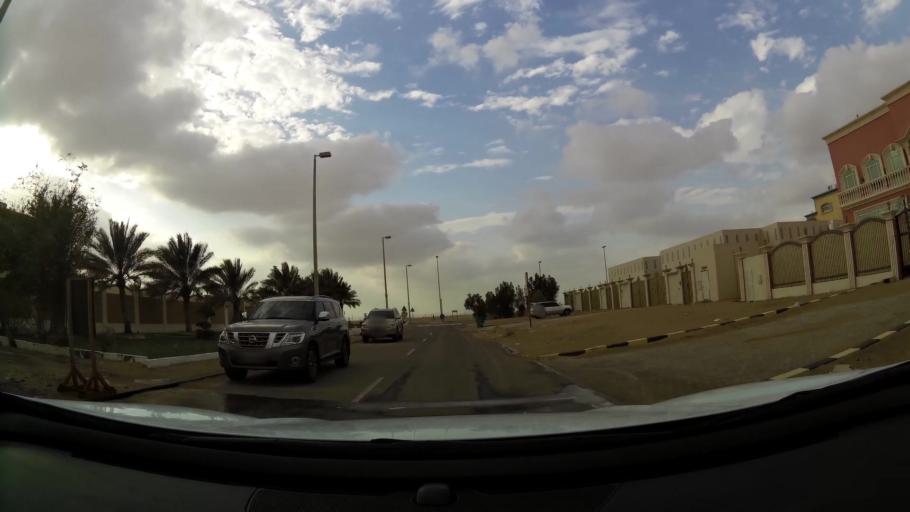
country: AE
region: Abu Dhabi
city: Abu Dhabi
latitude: 24.3535
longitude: 54.6114
